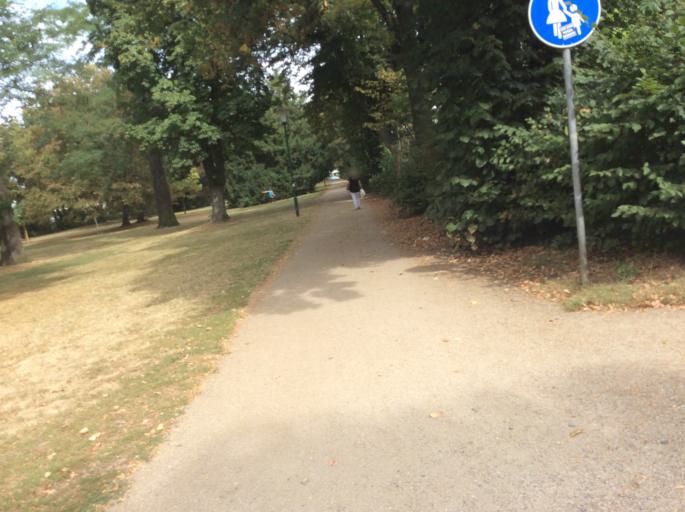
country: DE
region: Hesse
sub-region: Regierungsbezirk Darmstadt
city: Darmstadt
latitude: 49.8689
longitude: 8.6415
